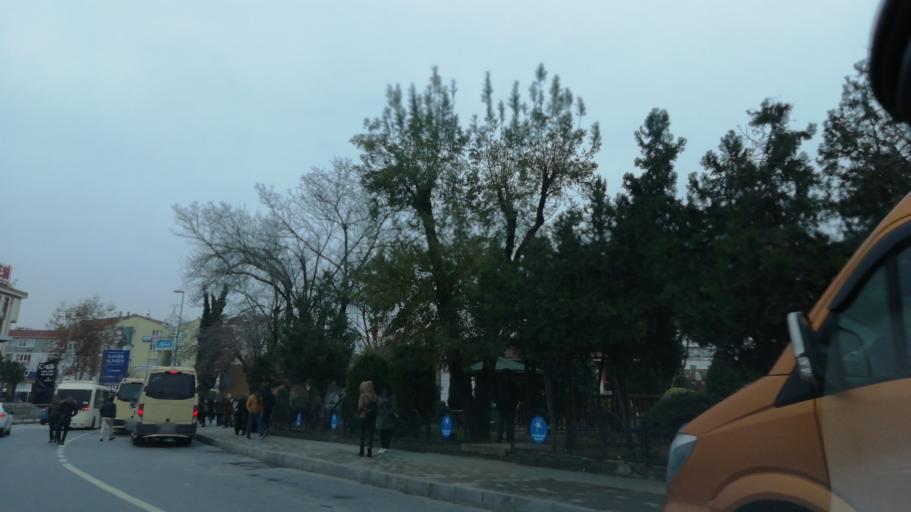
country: TR
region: Istanbul
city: Mahmutbey
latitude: 40.9990
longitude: 28.7971
